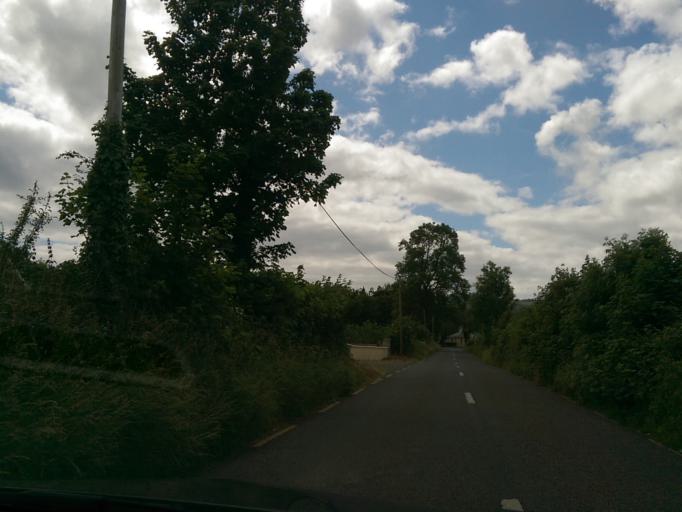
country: IE
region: Munster
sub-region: North Tipperary
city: Nenagh
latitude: 52.7991
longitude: -8.1909
